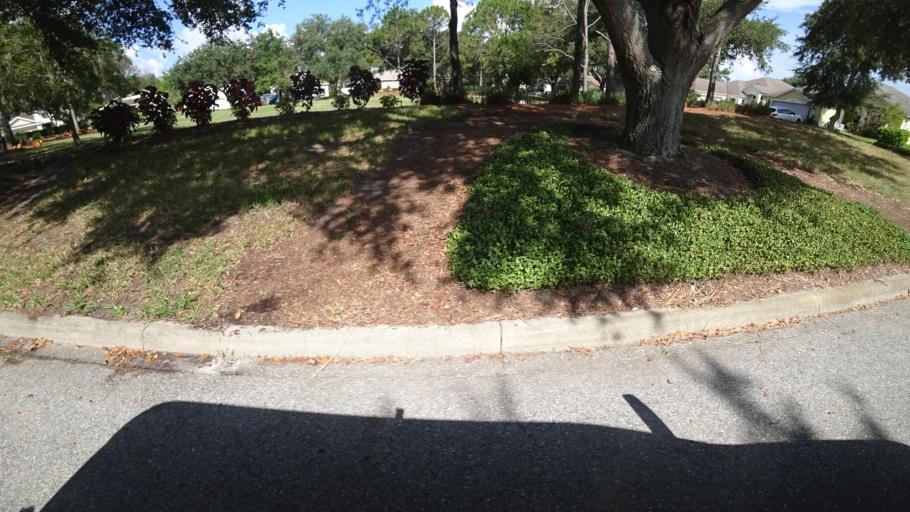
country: US
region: Florida
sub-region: Sarasota County
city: The Meadows
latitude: 27.4299
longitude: -82.4155
